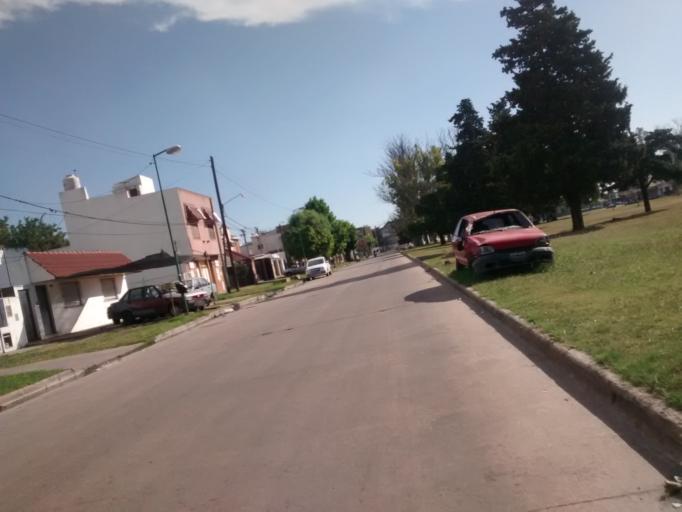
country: AR
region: Buenos Aires
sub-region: Partido de La Plata
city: La Plata
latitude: -34.9522
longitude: -57.9502
